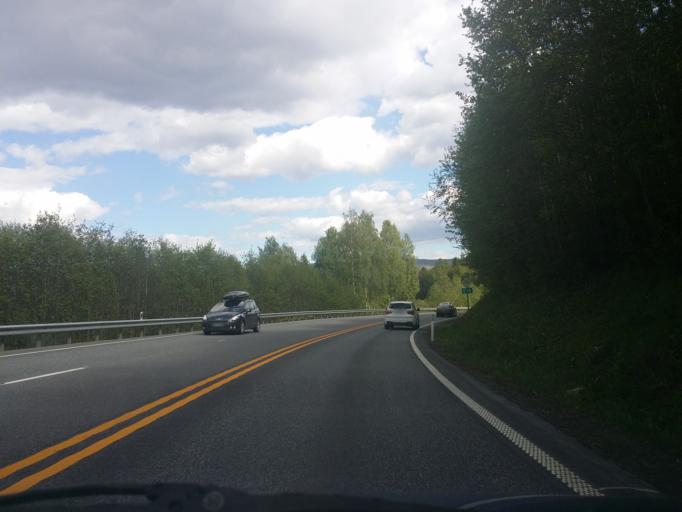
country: NO
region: Oppland
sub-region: Lunner
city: Roa
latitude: 60.2950
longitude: 10.5955
